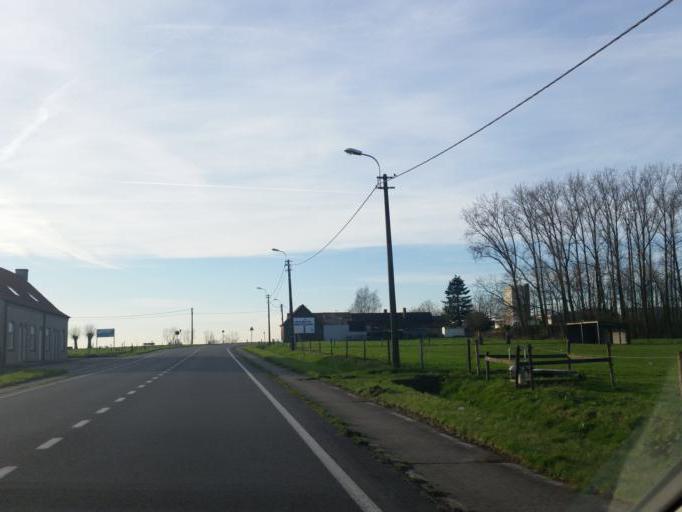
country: BE
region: Flanders
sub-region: Provincie Oost-Vlaanderen
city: Aalter
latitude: 51.1354
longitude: 3.4954
